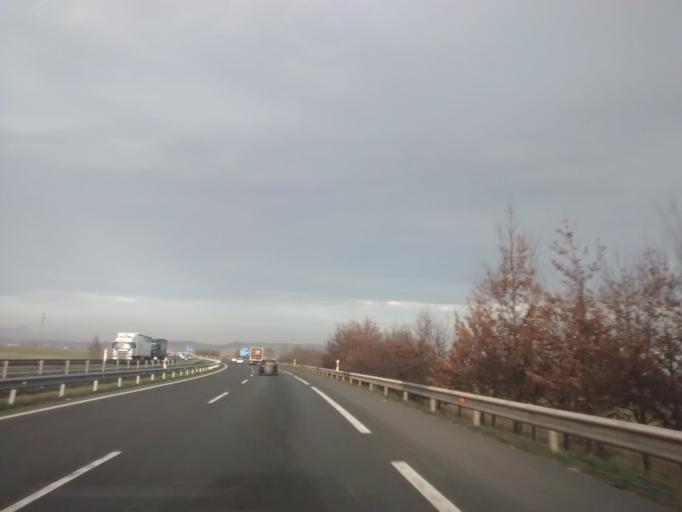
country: ES
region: Basque Country
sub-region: Provincia de Alava
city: Gasteiz / Vitoria
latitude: 42.8694
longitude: -2.7222
